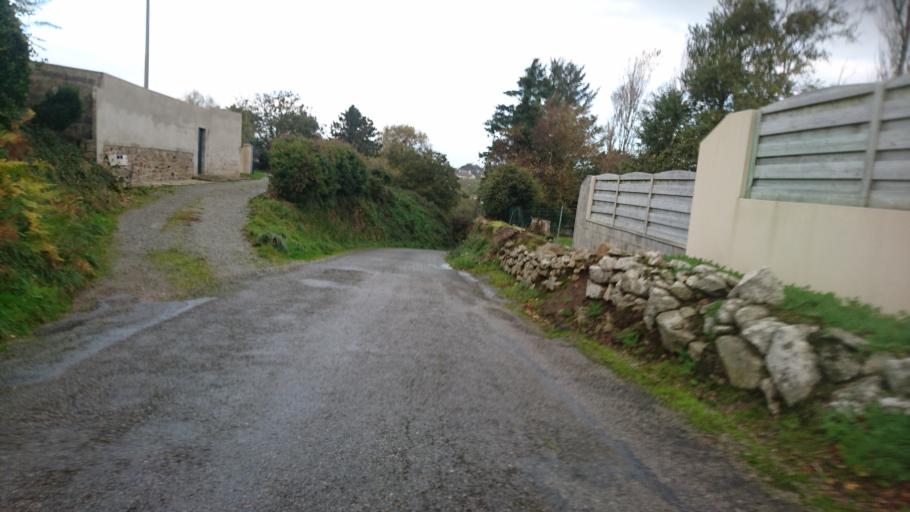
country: FR
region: Brittany
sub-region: Departement du Finistere
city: Lampaul-Plouarzel
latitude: 48.4417
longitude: -4.7679
